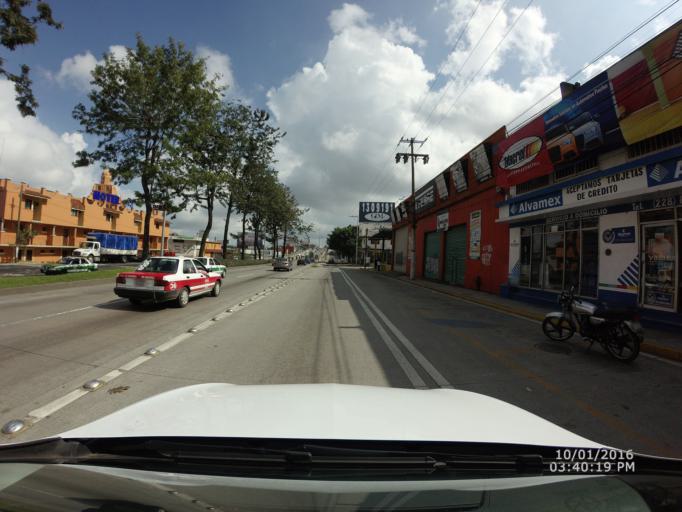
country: MX
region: Veracruz
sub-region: Xalapa
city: Xalapa de Enriquez
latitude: 19.5549
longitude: -96.9147
